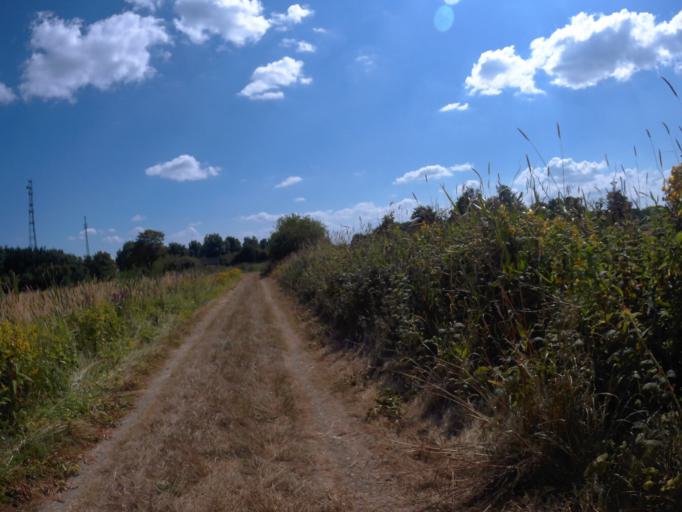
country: DE
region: Schleswig-Holstein
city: Suderstapel
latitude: 54.3636
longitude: 9.2207
